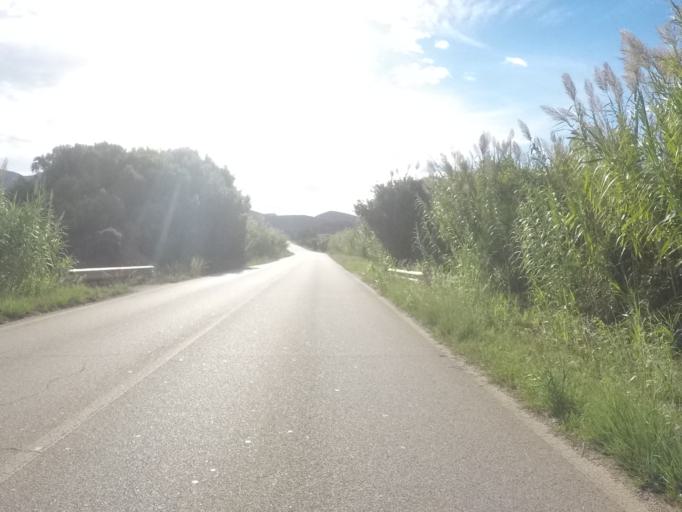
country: IT
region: Sardinia
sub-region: Provincia di Carbonia-Iglesias
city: Gonnesa
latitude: 39.2837
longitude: 8.4469
